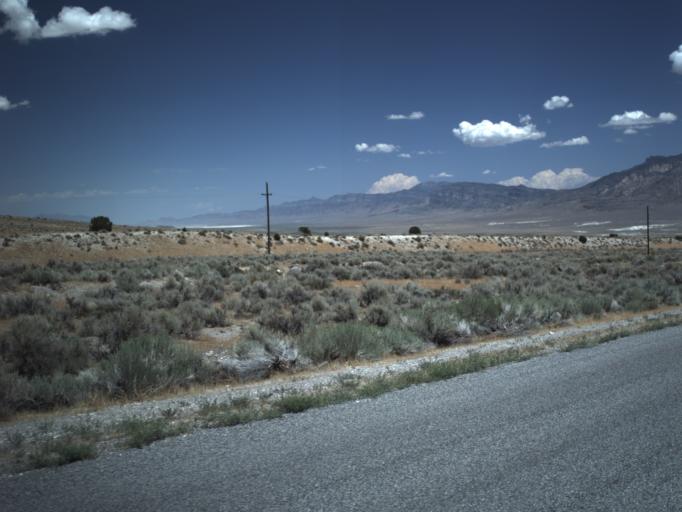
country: US
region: Utah
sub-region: Beaver County
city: Milford
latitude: 39.0861
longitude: -113.5586
